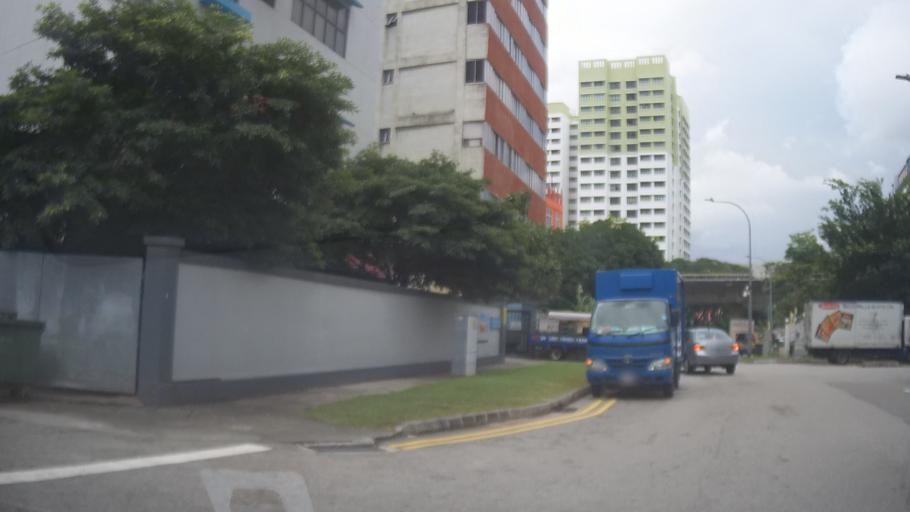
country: SG
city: Singapore
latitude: 1.3150
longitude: 103.8805
